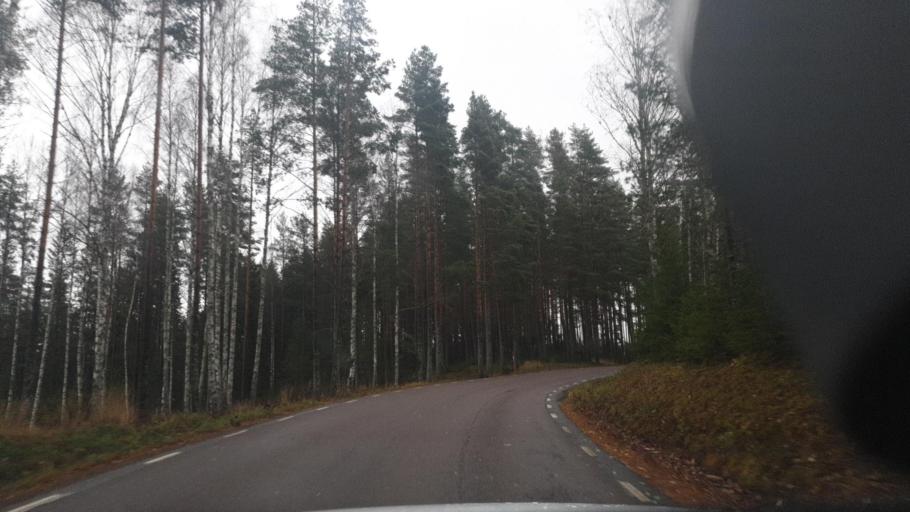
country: SE
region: Vaermland
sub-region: Eda Kommun
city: Charlottenberg
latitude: 59.7912
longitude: 12.2251
